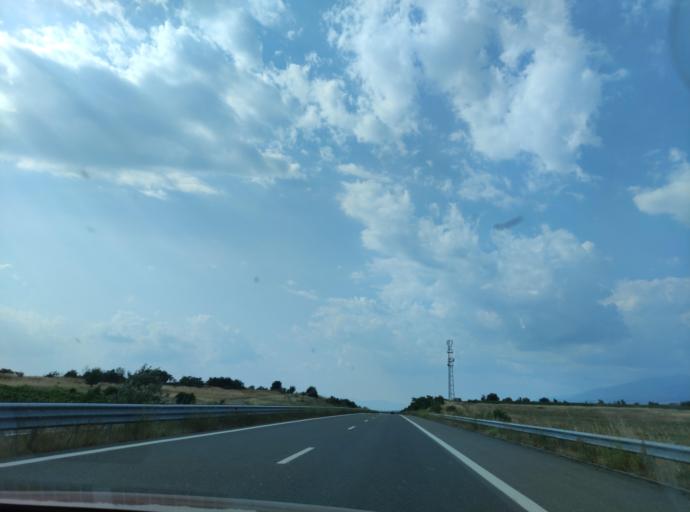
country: BG
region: Blagoevgrad
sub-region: Obshtina Sandanski
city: Sandanski
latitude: 41.4696
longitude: 23.3133
